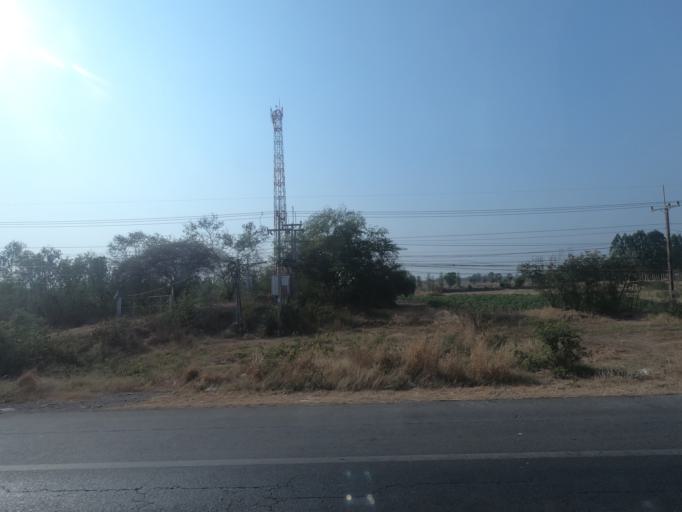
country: TH
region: Khon Kaen
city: Ban Haet
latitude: 16.2630
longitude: 102.7781
